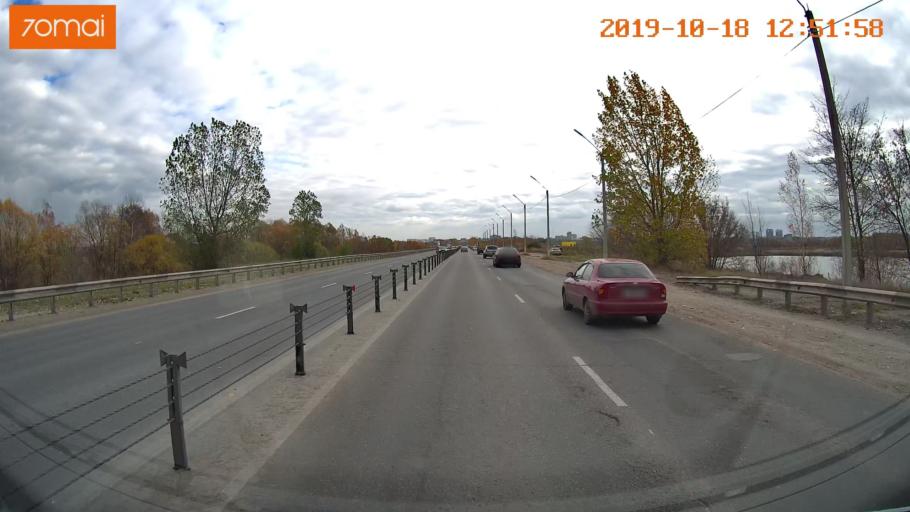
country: RU
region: Rjazan
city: Ryazan'
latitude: 54.6561
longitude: 39.6880
